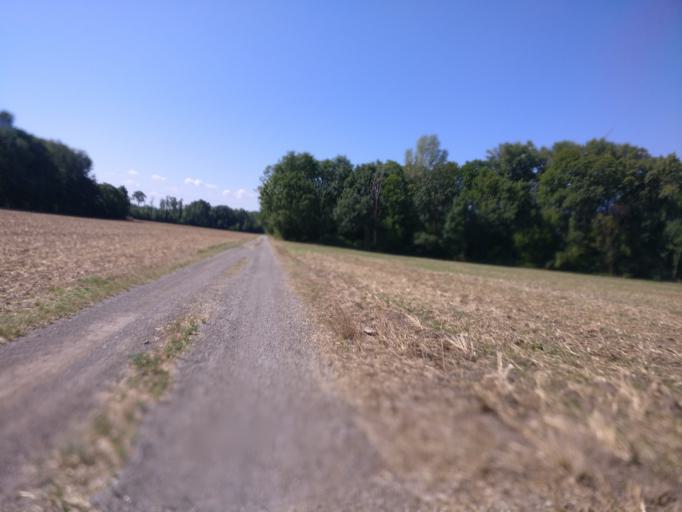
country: AT
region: Lower Austria
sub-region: Politischer Bezirk Baden
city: Pottendorf
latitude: 47.9298
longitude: 16.3697
